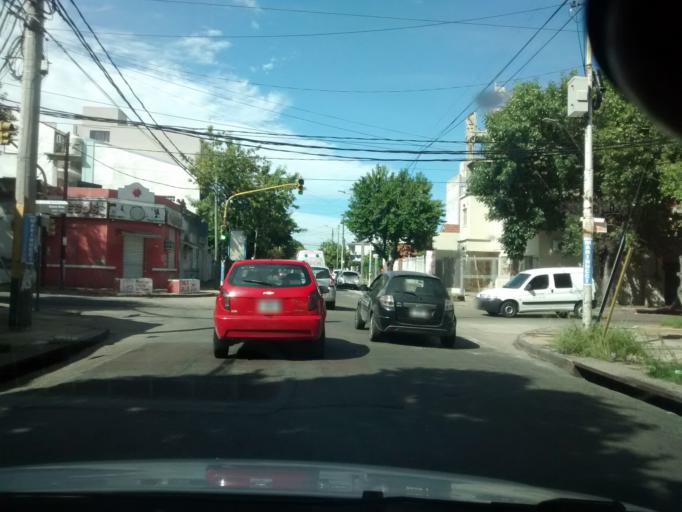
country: AR
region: Buenos Aires
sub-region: Partido de Moron
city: Moron
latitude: -34.6569
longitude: -58.6228
